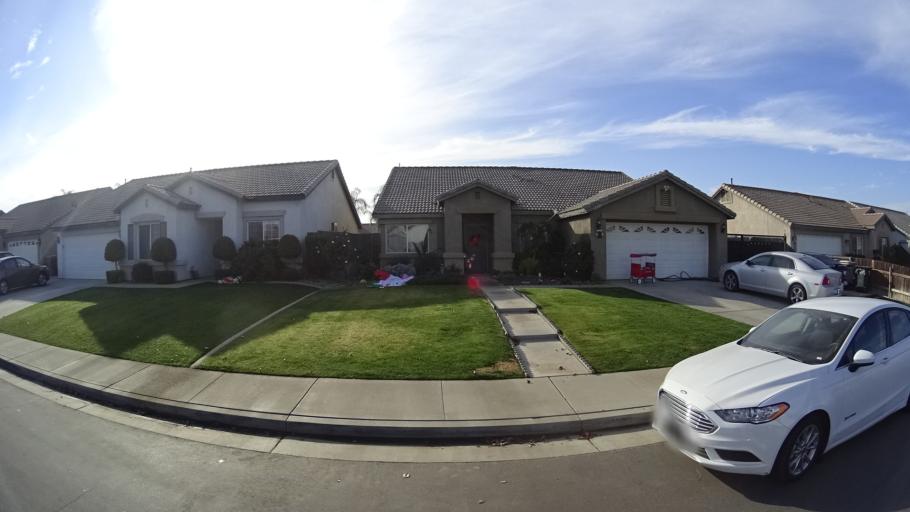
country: US
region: California
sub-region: Kern County
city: Rosedale
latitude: 35.4020
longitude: -119.1377
